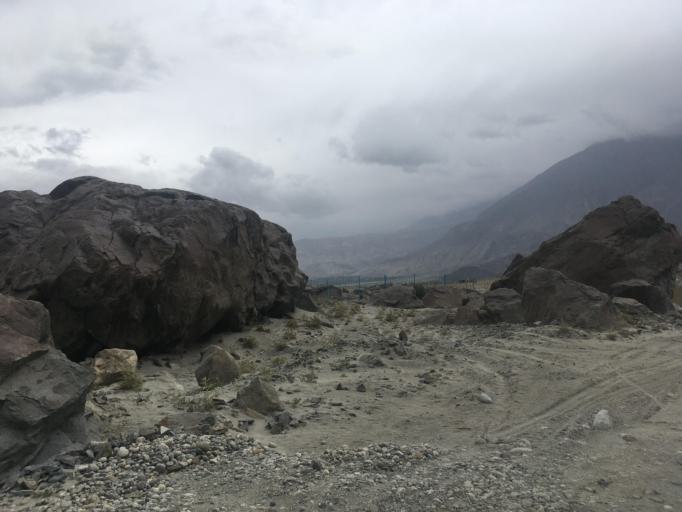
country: PK
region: Gilgit-Baltistan
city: Skardu
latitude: 35.3196
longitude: 75.6558
